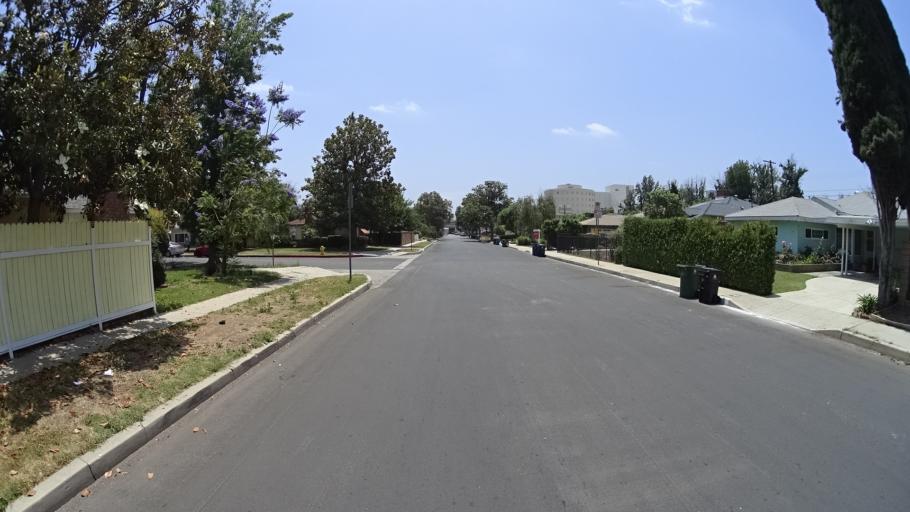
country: US
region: California
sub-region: Los Angeles County
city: Van Nuys
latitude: 34.1974
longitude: -118.4618
